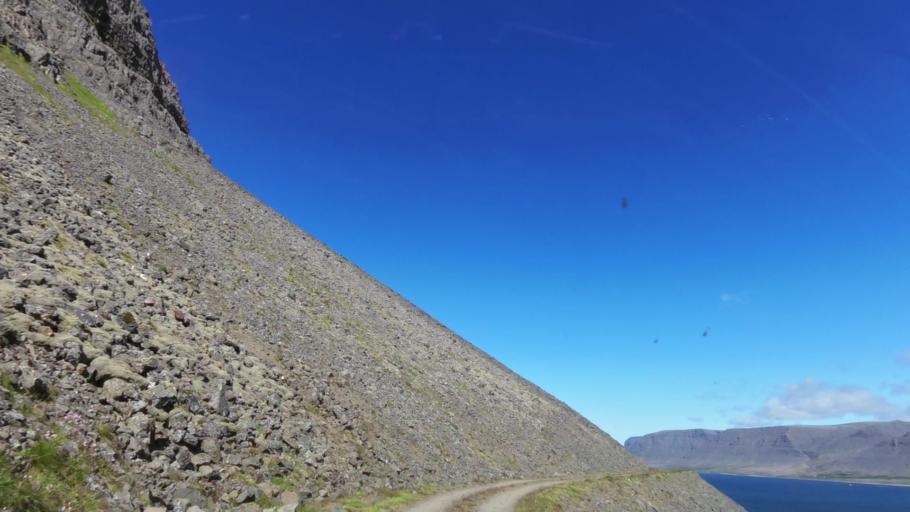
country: IS
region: West
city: Olafsvik
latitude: 65.6316
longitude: -23.9159
